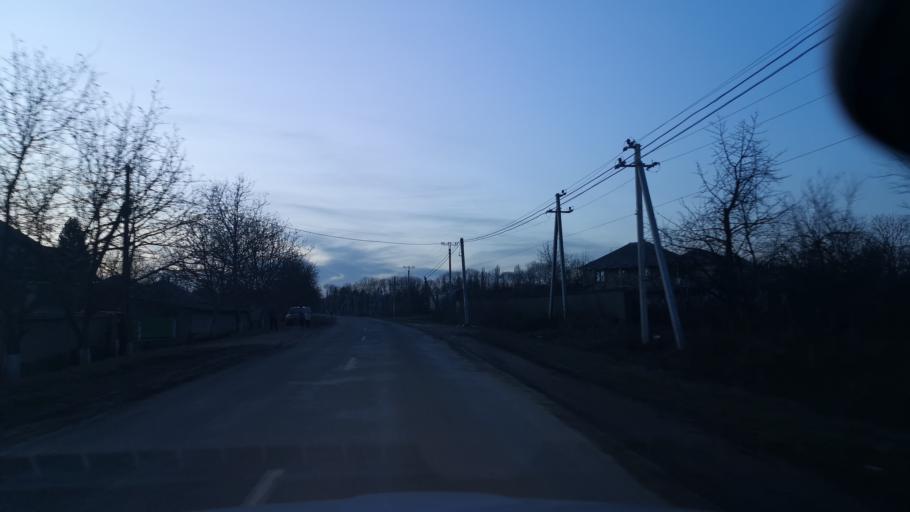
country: MD
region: Orhei
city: Orhei
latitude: 47.2872
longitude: 28.8682
